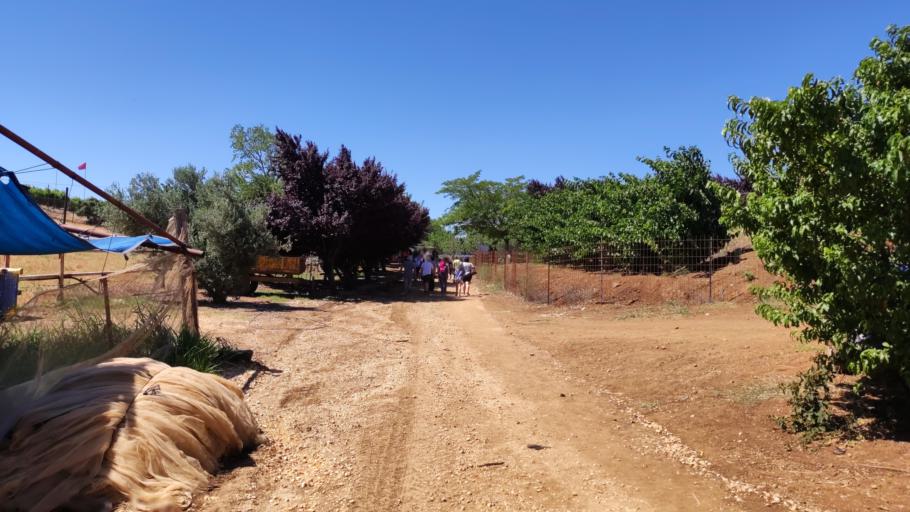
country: SY
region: Quneitra
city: Al Qunaytirah
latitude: 33.1187
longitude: 35.8065
